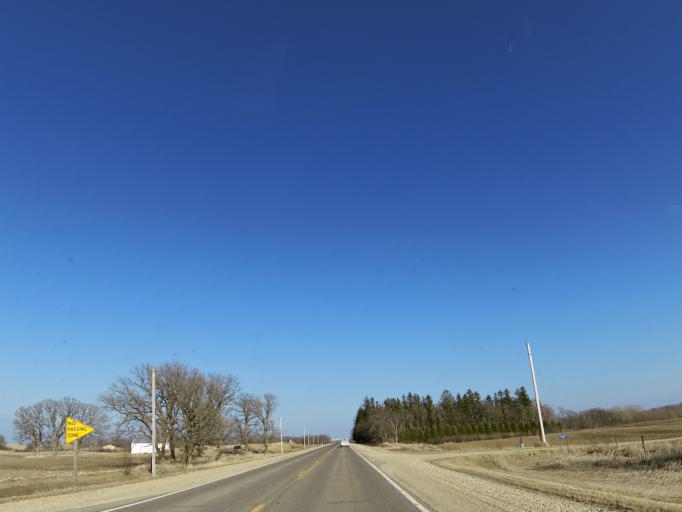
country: US
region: Iowa
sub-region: Worth County
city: Northwood
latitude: 43.4443
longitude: -93.2760
